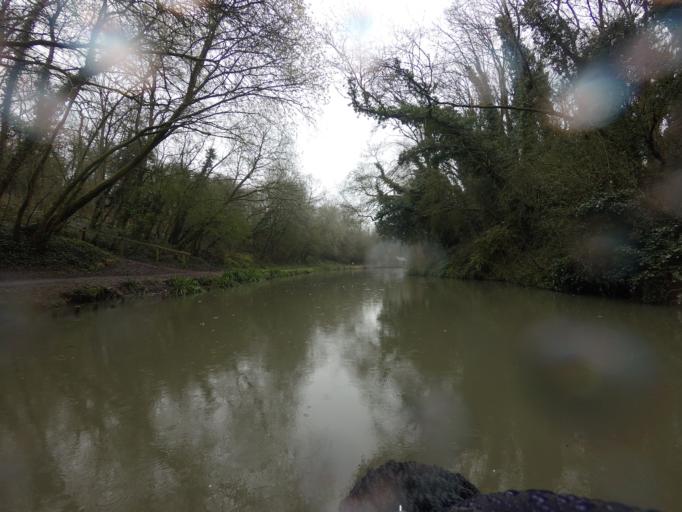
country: GB
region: England
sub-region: Northamptonshire
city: Blisworth
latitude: 52.1706
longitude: -0.9367
